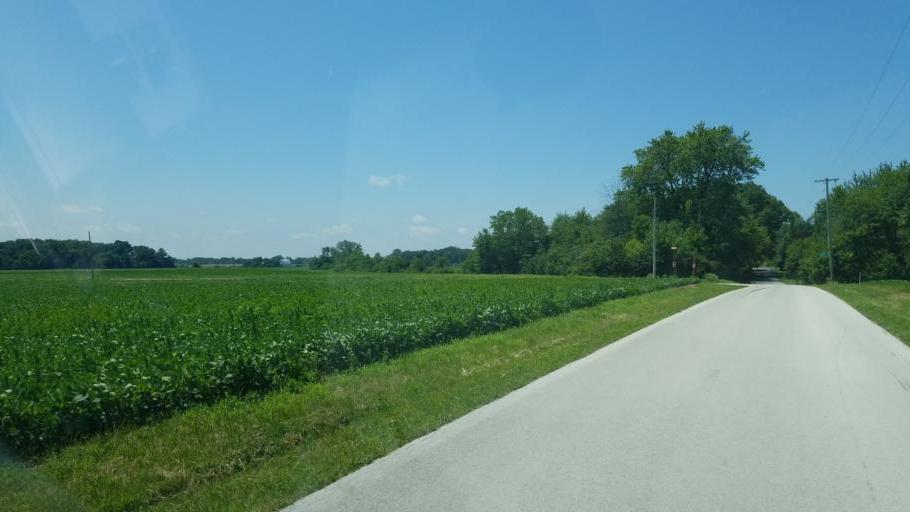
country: US
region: Ohio
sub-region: Sandusky County
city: Fremont
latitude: 41.4035
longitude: -83.0767
